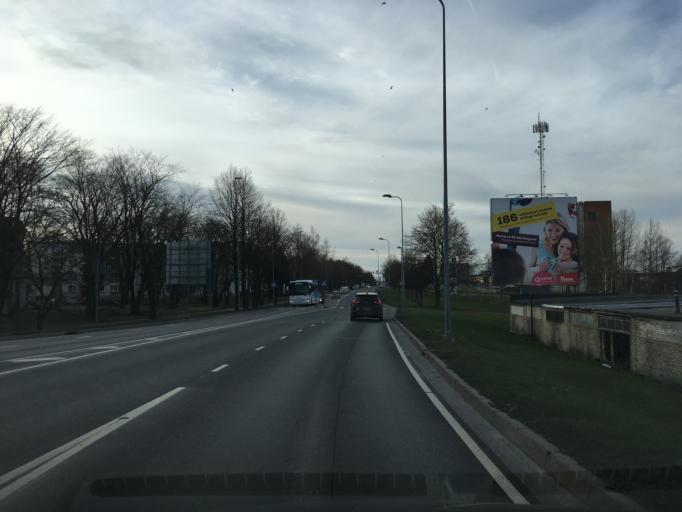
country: EE
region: Ida-Virumaa
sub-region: Johvi vald
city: Johvi
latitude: 59.3540
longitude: 27.4160
